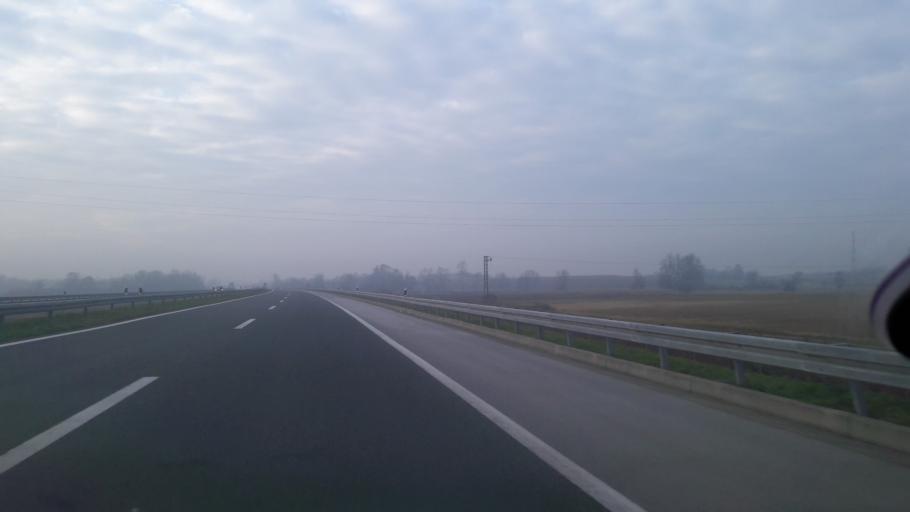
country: HR
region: Osjecko-Baranjska
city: Piskorevci
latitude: 45.3098
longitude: 18.3662
